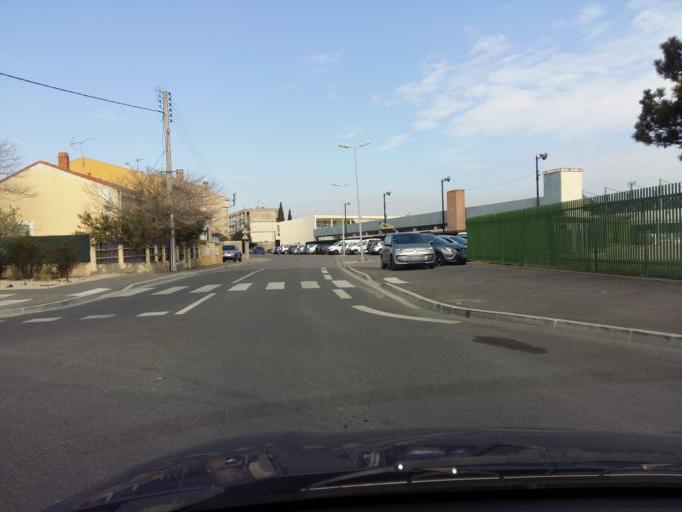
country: FR
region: Provence-Alpes-Cote d'Azur
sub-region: Departement des Bouches-du-Rhone
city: Salon-de-Provence
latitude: 43.6357
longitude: 5.0906
